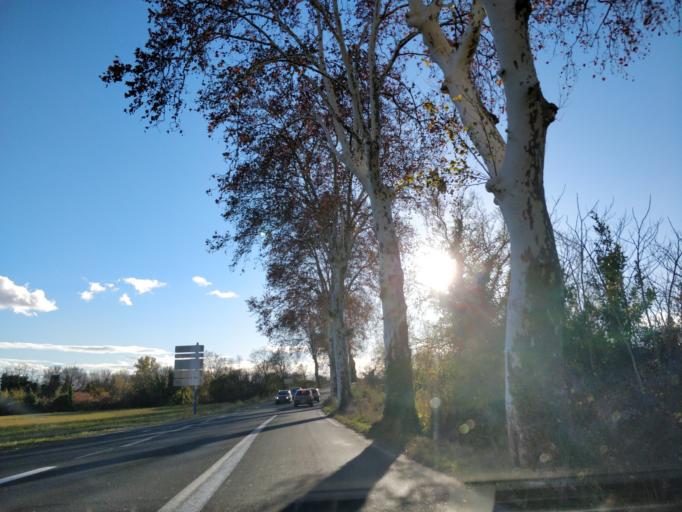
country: FR
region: Languedoc-Roussillon
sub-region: Departement de l'Herault
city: Castries
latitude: 43.6734
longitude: 3.9819
